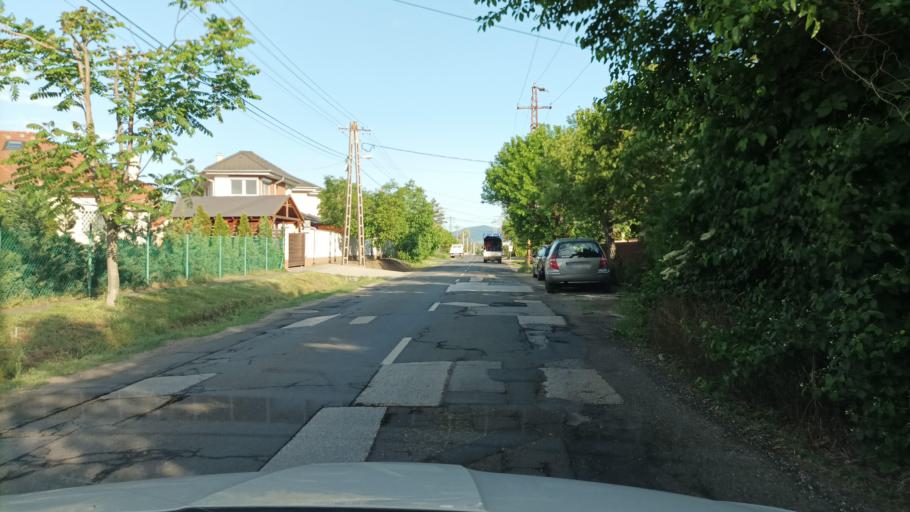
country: HU
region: Pest
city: Dunakeszi
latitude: 47.6552
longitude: 19.1274
